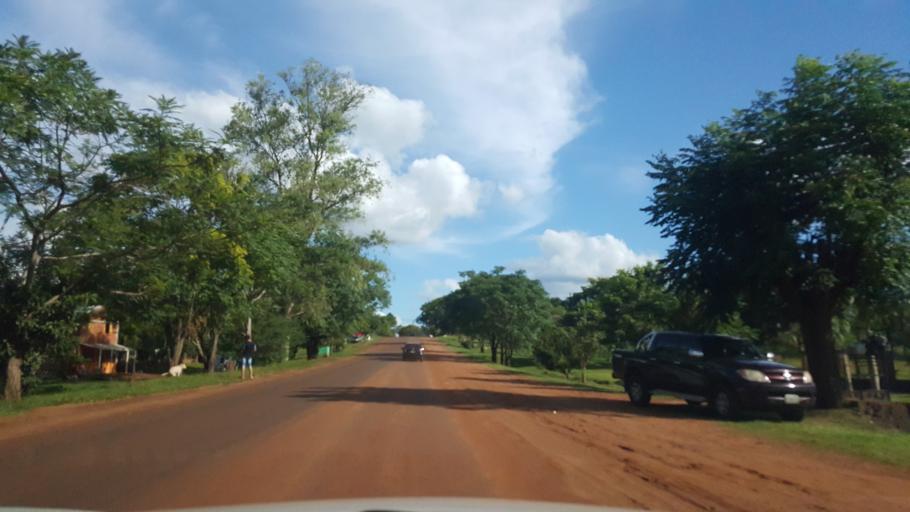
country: AR
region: Misiones
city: Santa Ana
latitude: -27.3637
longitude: -55.5859
